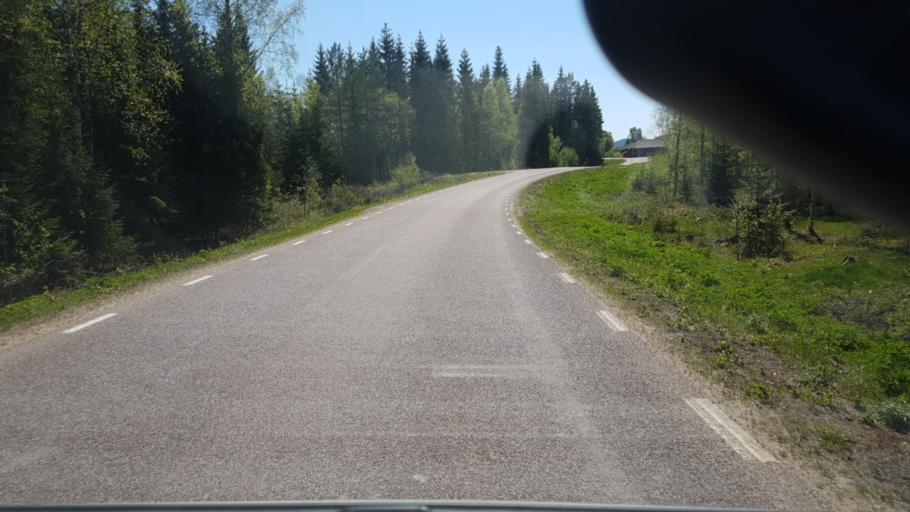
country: SE
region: Vaermland
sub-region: Arvika Kommun
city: Arvika
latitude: 59.7574
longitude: 12.8234
